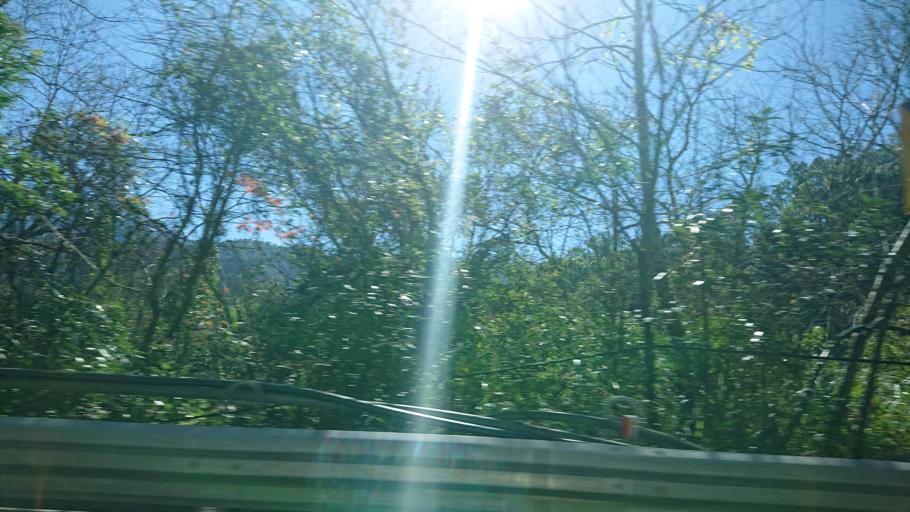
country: TW
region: Taiwan
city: Daxi
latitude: 24.4125
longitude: 121.3598
